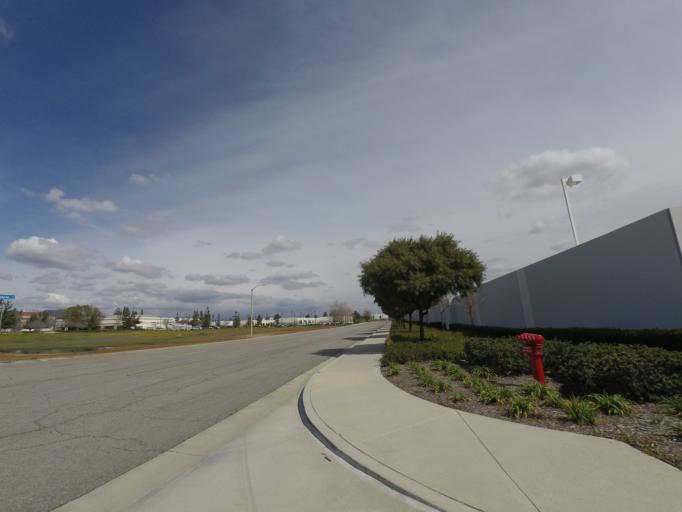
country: US
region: California
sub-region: Riverside County
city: March Air Force Base
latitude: 33.9127
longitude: -117.2650
